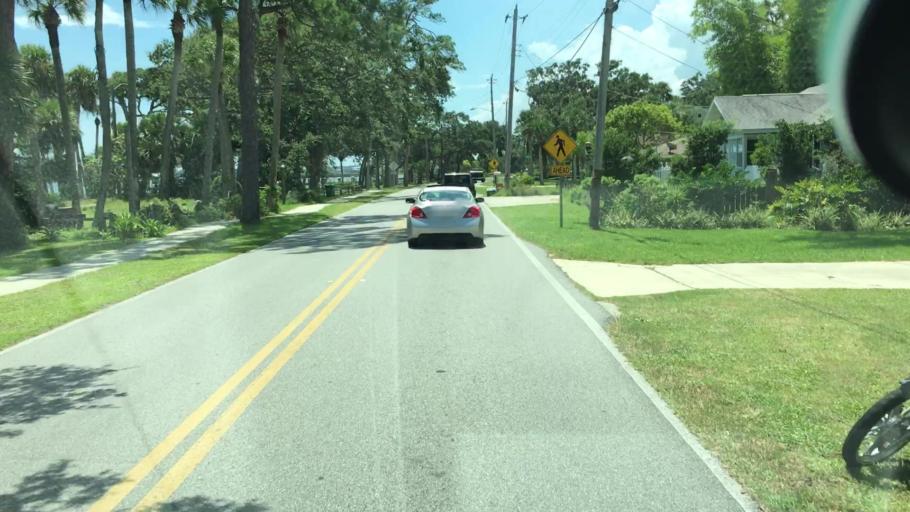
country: US
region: Florida
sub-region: Volusia County
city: Holly Hill
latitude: 29.2537
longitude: -81.0392
